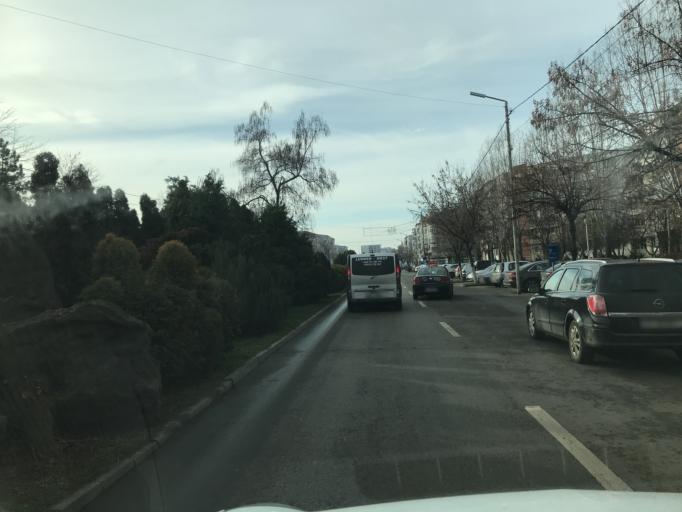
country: RO
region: Olt
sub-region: Municipiul Slatina
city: Slatina
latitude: 44.4280
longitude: 24.3841
